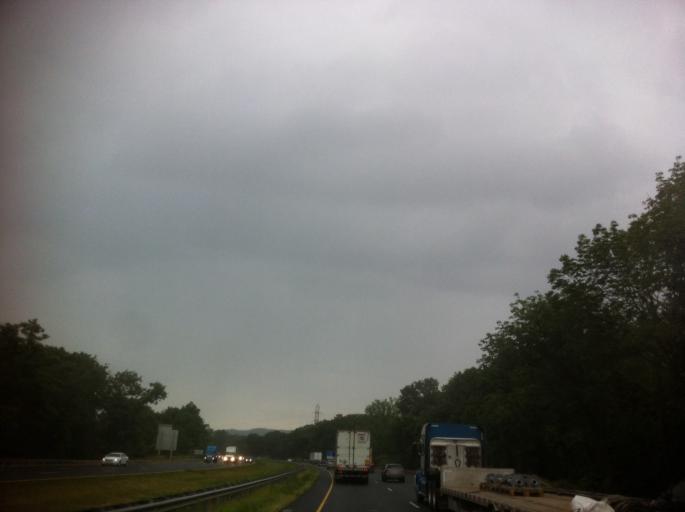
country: US
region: New Jersey
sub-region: Morris County
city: Rockaway
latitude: 40.9114
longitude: -74.5128
